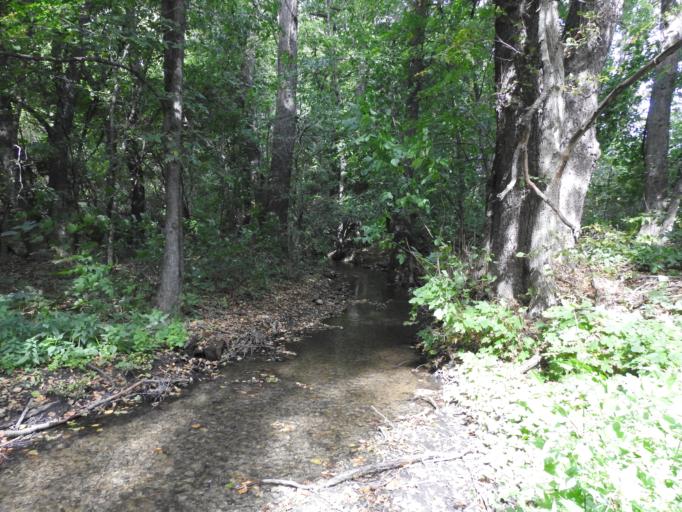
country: RU
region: Saratov
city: Novyye Burasy
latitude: 52.1464
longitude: 46.2321
